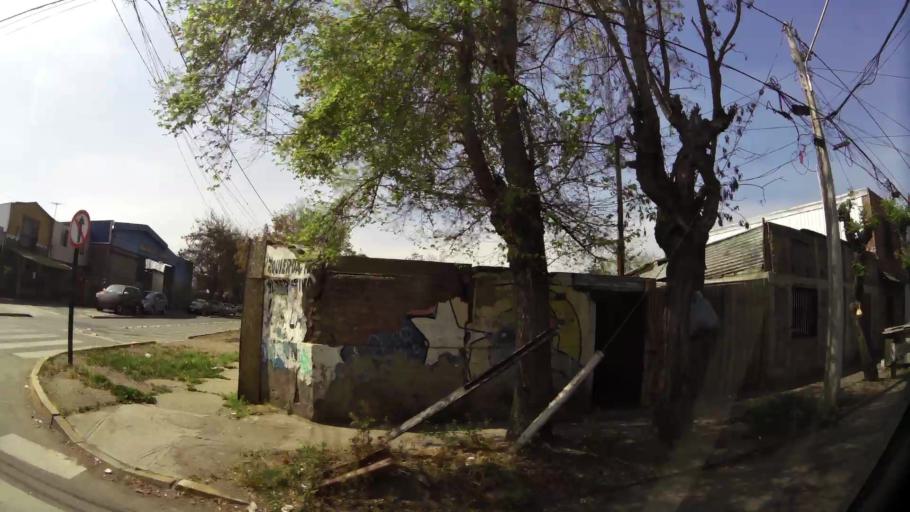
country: CL
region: Santiago Metropolitan
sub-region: Provincia de Santiago
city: Lo Prado
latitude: -33.4240
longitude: -70.7244
